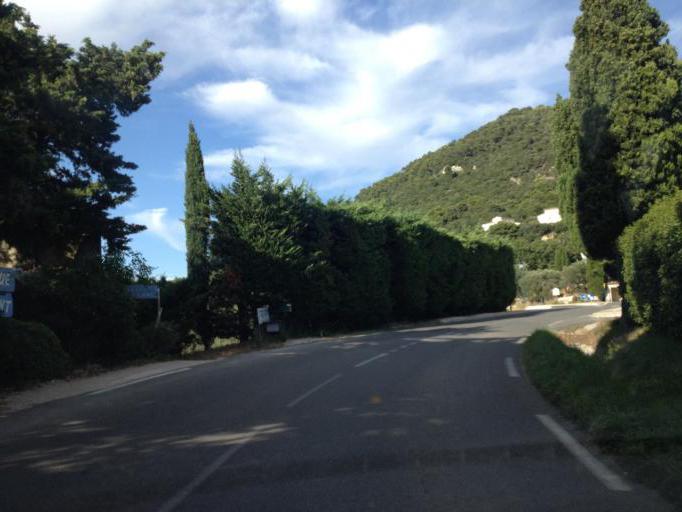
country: FR
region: Provence-Alpes-Cote d'Azur
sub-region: Departement du Vaucluse
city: Sablet
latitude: 44.2069
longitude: 5.0183
